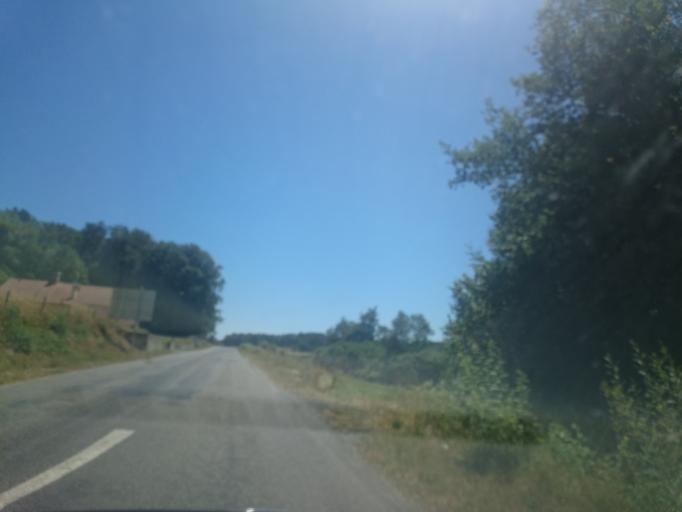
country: FR
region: Auvergne
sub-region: Departement du Cantal
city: Laroquebrou
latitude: 44.8861
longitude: 2.2122
